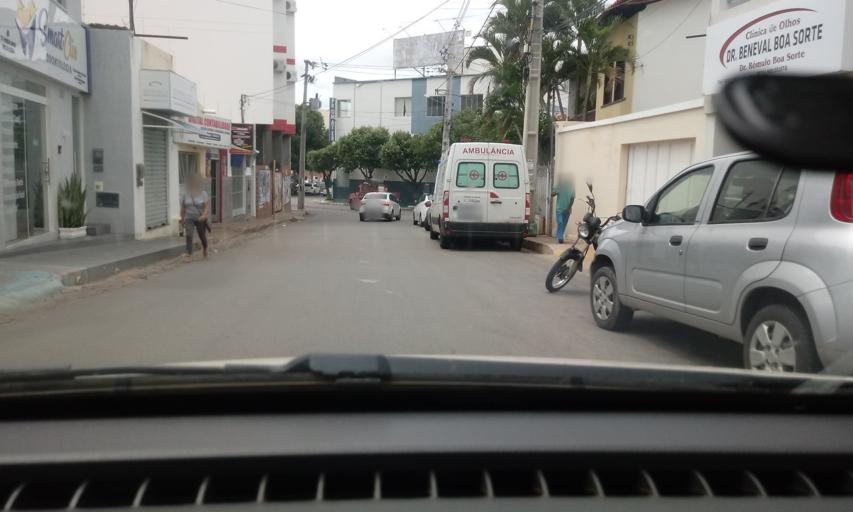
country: BR
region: Bahia
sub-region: Guanambi
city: Guanambi
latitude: -14.2262
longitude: -42.7814
